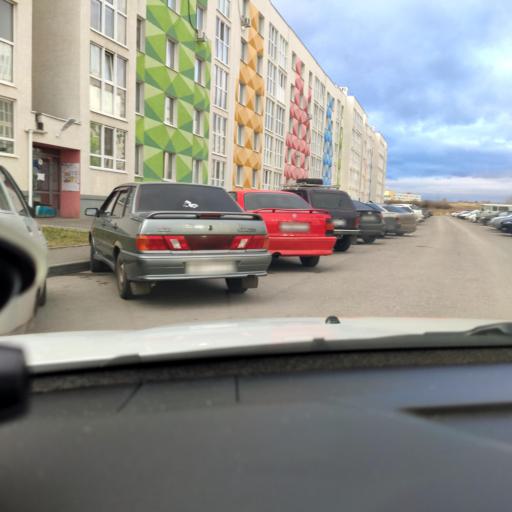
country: RU
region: Samara
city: Petra-Dubrava
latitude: 53.3012
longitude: 50.3334
